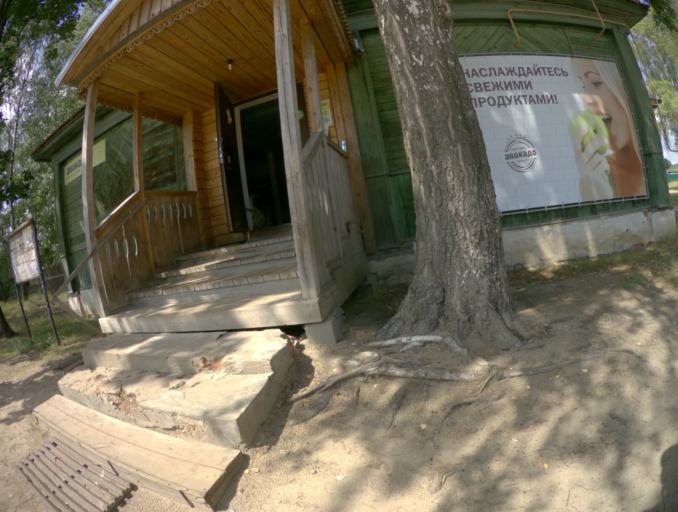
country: RU
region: Ivanovo
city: Yuzha
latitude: 56.5283
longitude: 42.1635
